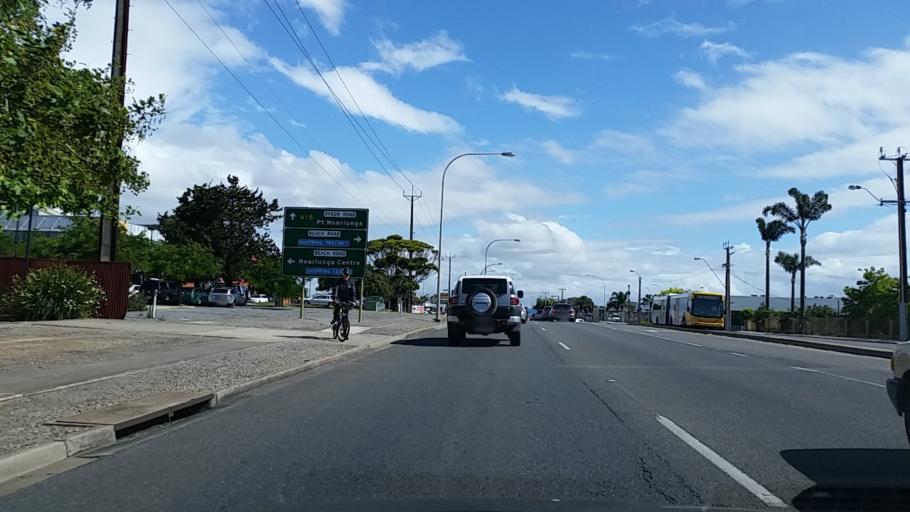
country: AU
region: South Australia
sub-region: Adelaide
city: Port Noarlunga
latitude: -35.1369
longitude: 138.4862
